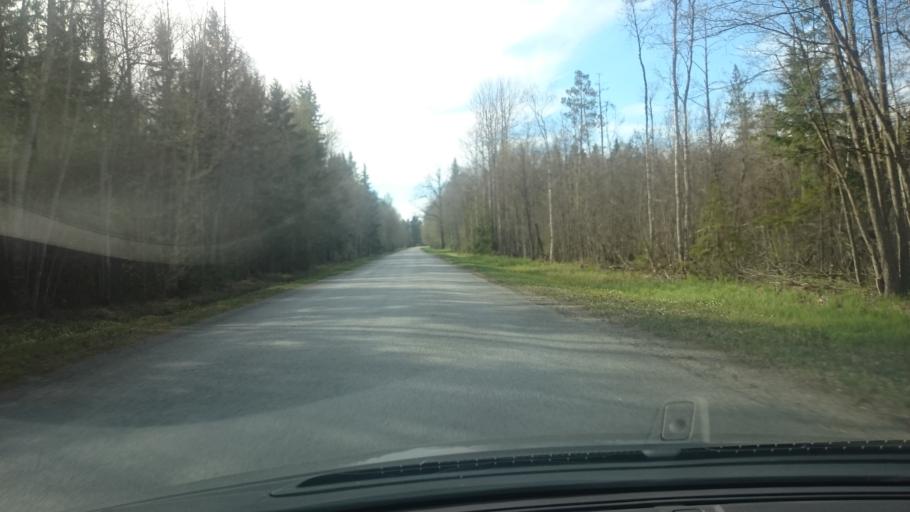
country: EE
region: Ida-Virumaa
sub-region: Sillamaee linn
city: Sillamae
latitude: 59.0821
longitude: 27.6795
